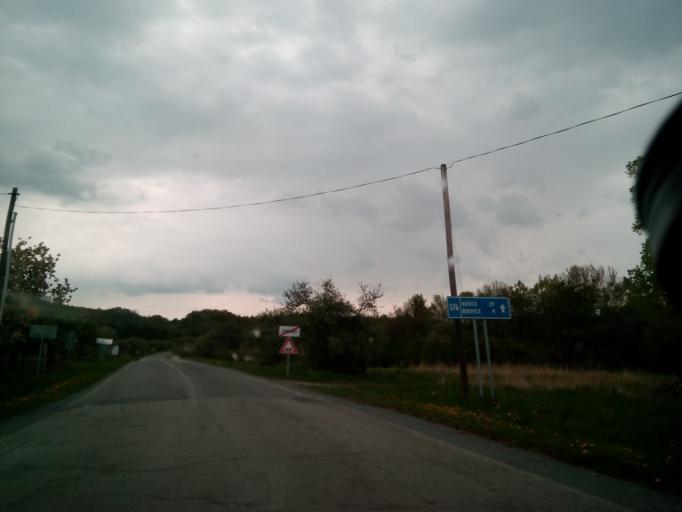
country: SK
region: Kosicky
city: Secovce
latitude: 48.7985
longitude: 21.4814
